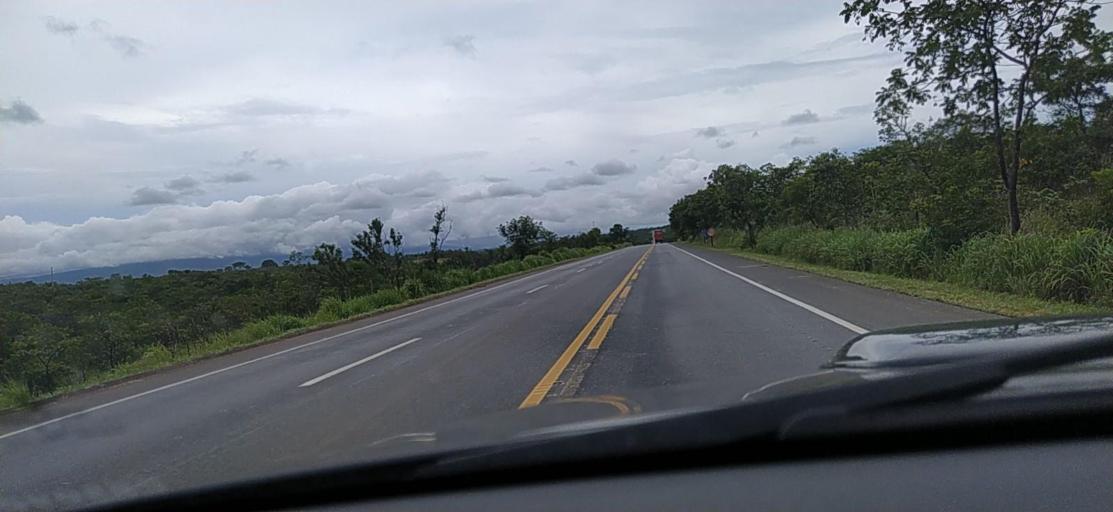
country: BR
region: Minas Gerais
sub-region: Corinto
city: Corinto
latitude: -18.3142
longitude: -44.4211
